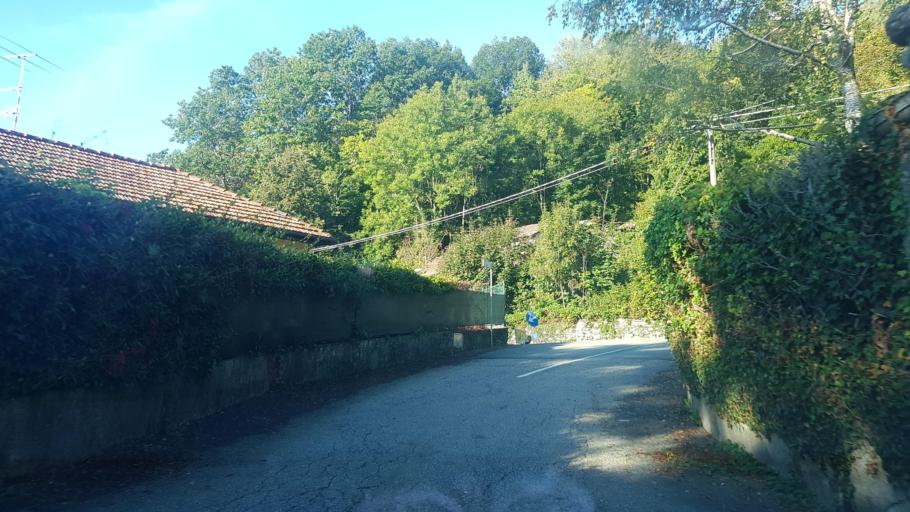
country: IT
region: Piedmont
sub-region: Provincia Verbano-Cusio-Ossola
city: Bee
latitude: 45.9738
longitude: 8.5829
